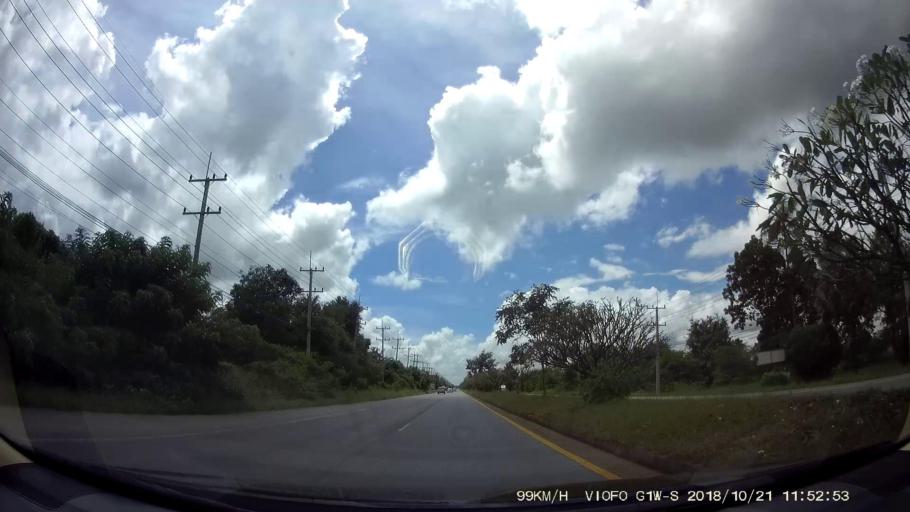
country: TH
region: Chaiyaphum
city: Chatturat
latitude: 15.6032
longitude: 101.9091
